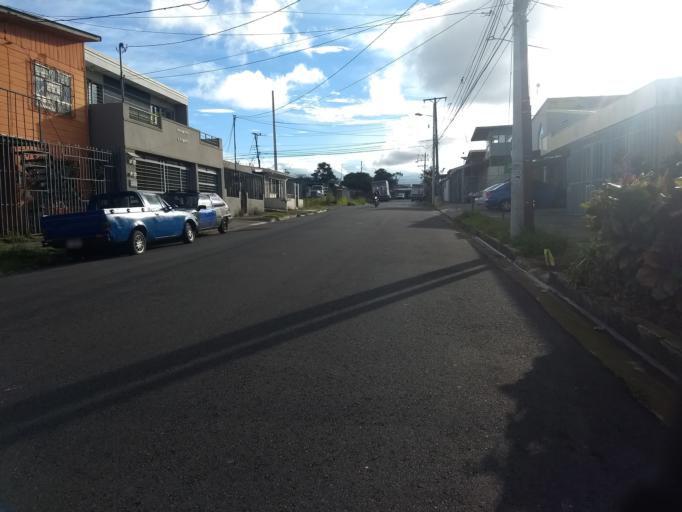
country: CR
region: San Jose
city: San Juan
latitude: 9.9572
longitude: -84.0824
